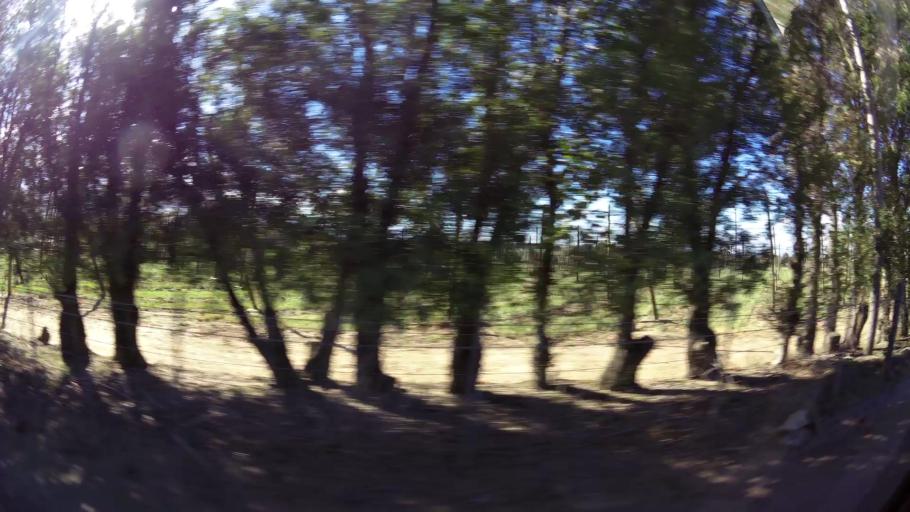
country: ZA
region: Western Cape
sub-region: Eden District Municipality
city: George
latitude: -33.9594
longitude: 22.3989
